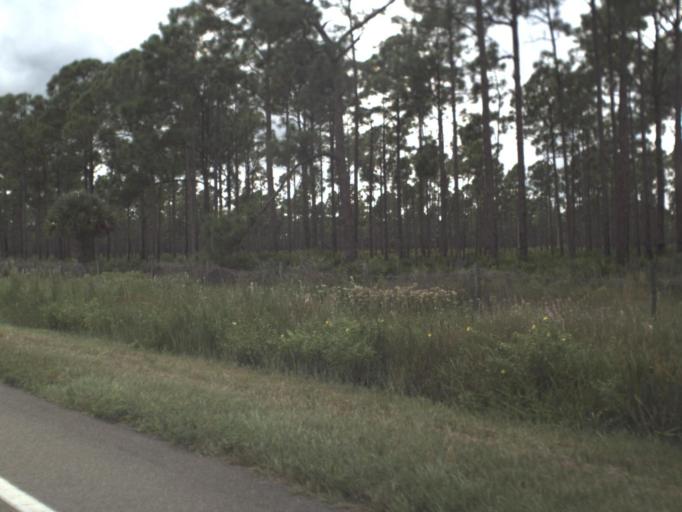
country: US
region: Florida
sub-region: Lee County
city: Olga
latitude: 26.8835
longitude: -81.7601
